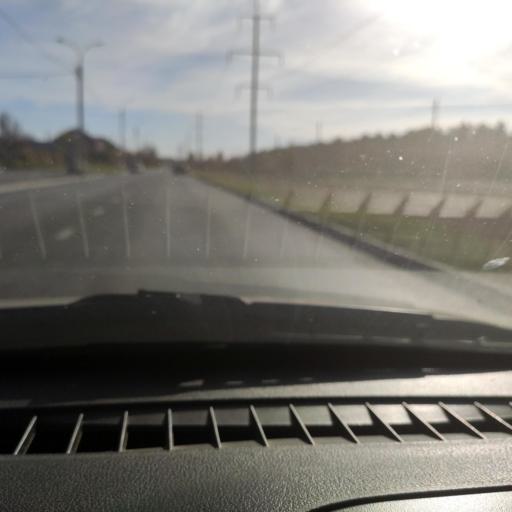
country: RU
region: Samara
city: Tol'yatti
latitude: 53.5202
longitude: 49.3938
